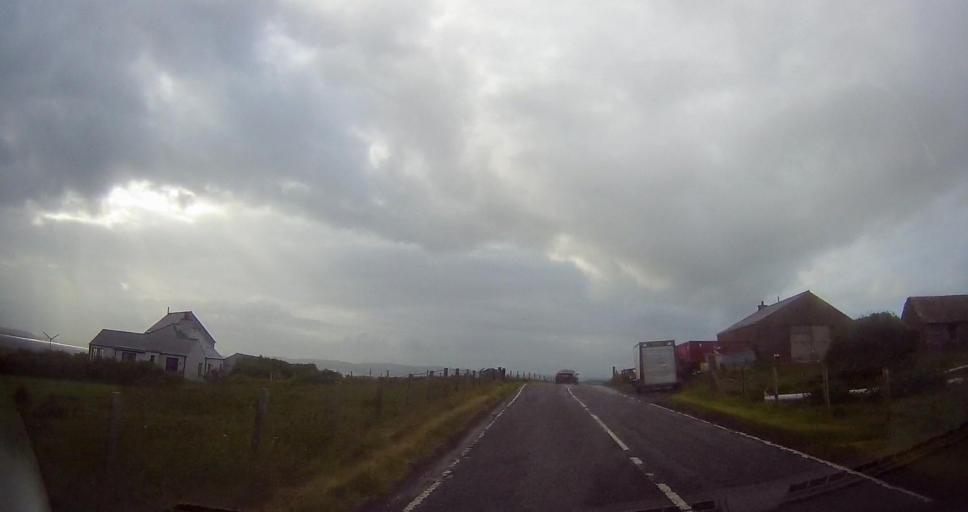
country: GB
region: Scotland
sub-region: Orkney Islands
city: Stromness
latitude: 58.9306
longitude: -3.2070
